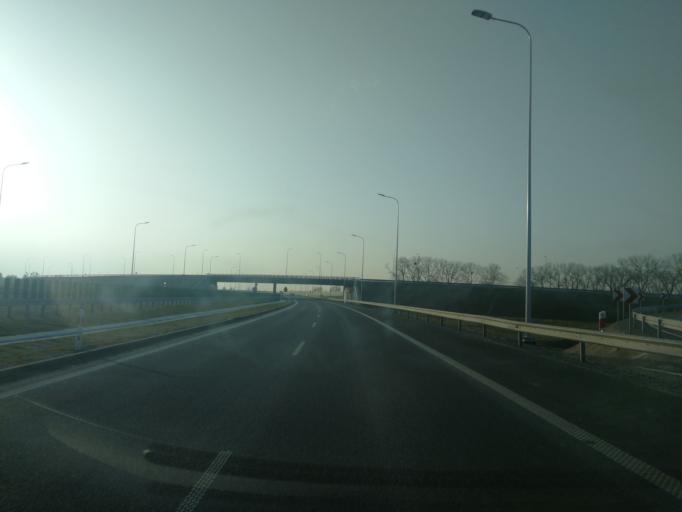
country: PL
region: Warmian-Masurian Voivodeship
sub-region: Powiat elblaski
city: Elblag
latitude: 54.1637
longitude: 19.3483
